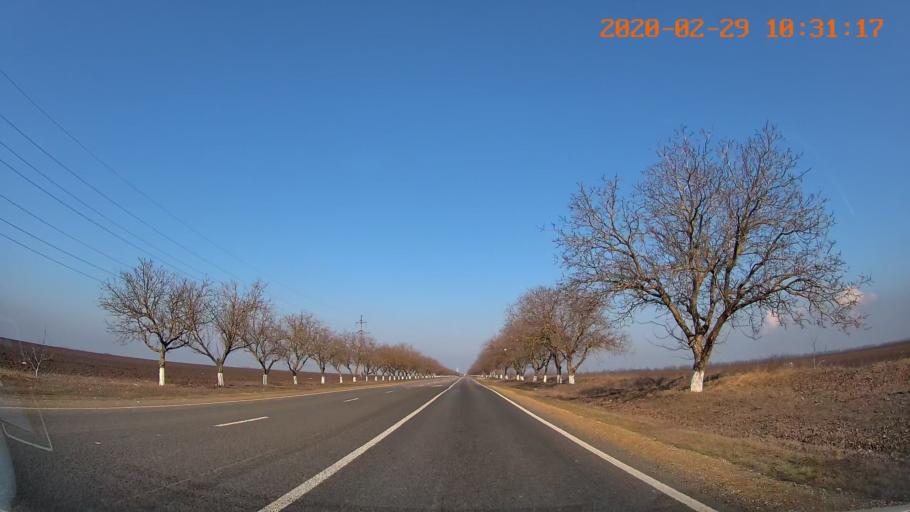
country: MD
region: Telenesti
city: Tiraspolul Nou
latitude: 46.9461
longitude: 29.5660
